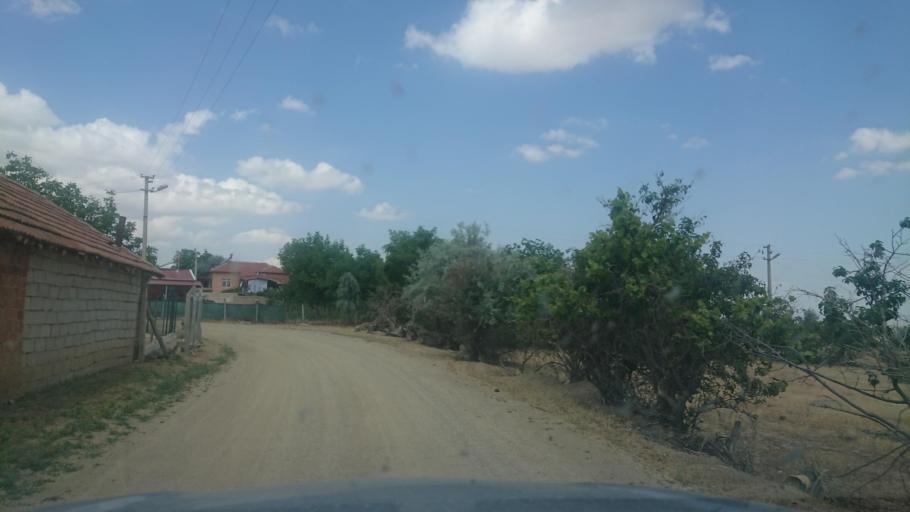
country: TR
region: Aksaray
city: Agacoren
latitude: 38.9347
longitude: 33.9513
